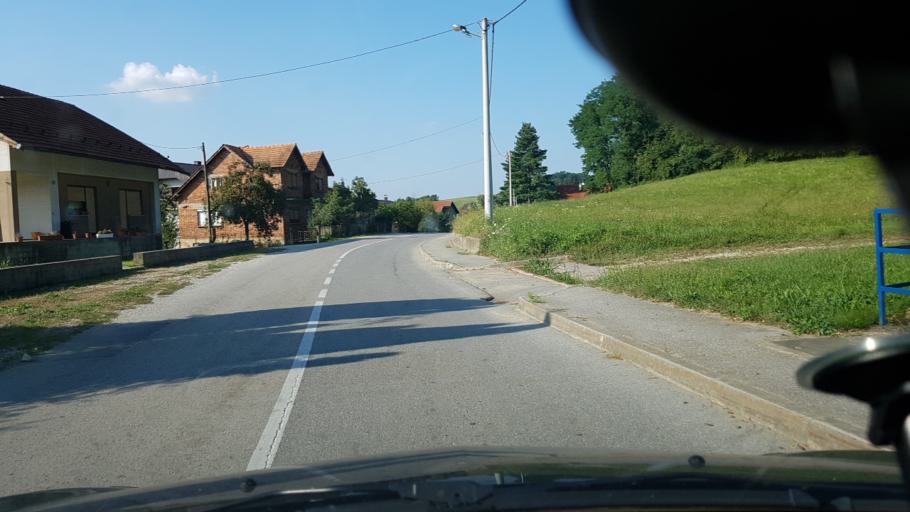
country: HR
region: Zagrebacka
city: Pojatno
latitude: 45.9464
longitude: 15.7307
